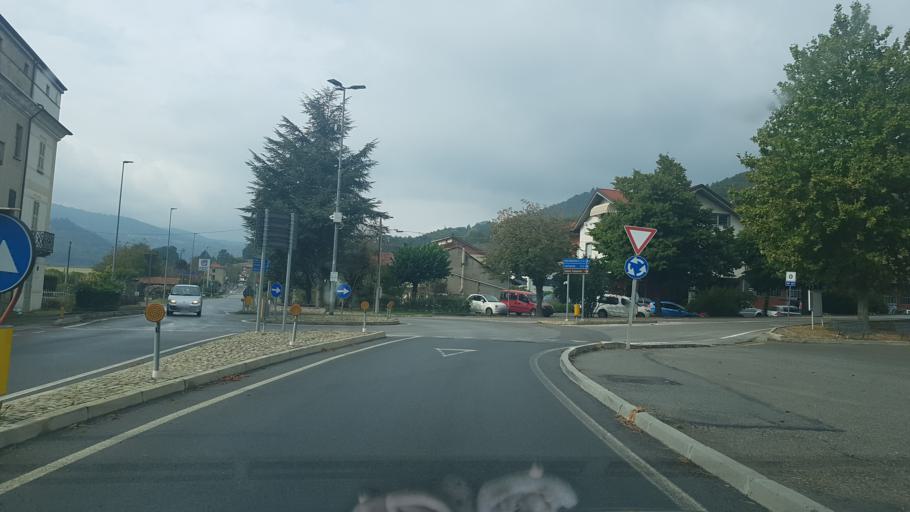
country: IT
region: Piedmont
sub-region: Provincia di Cuneo
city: Camerana
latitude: 44.4451
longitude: 8.1425
